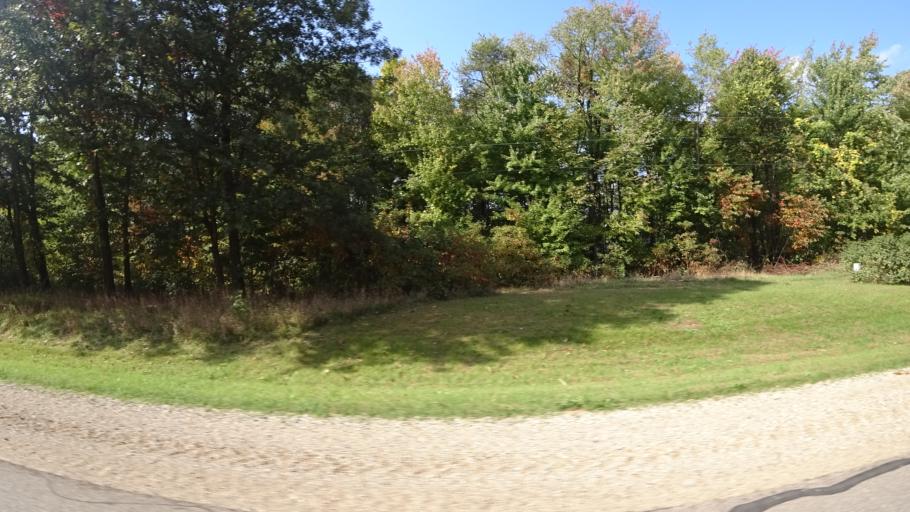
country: US
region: Michigan
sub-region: Saint Joseph County
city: Centreville
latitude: 42.0036
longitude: -85.5547
